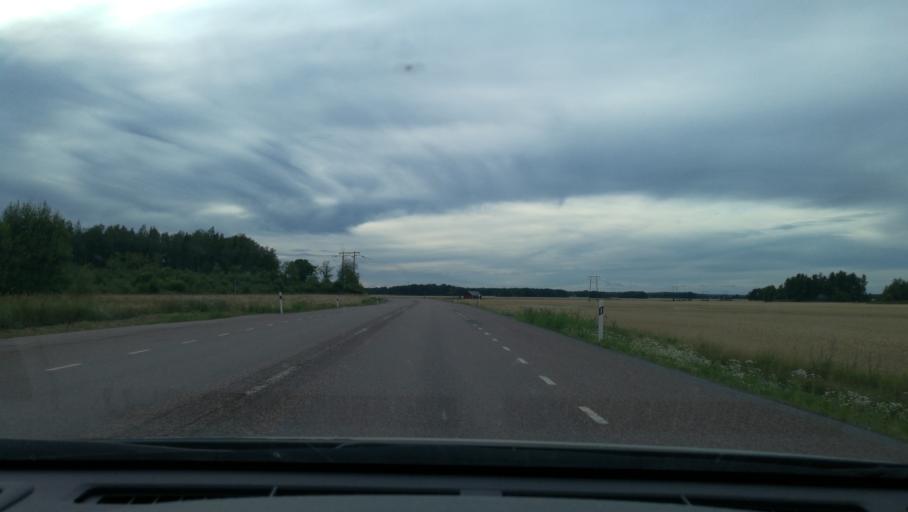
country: SE
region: Vaestmanland
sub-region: Kopings Kommun
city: Koping
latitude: 59.4543
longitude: 16.0257
